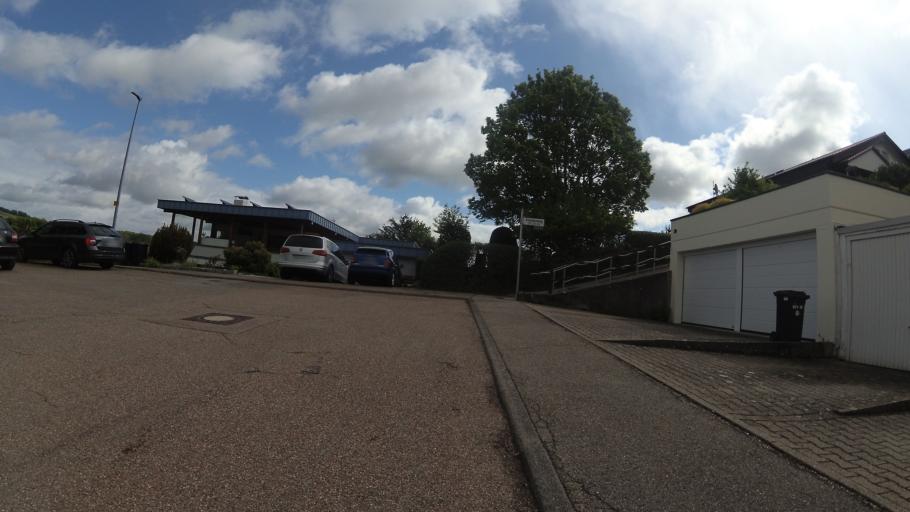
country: DE
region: Baden-Wuerttemberg
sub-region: Regierungsbezirk Stuttgart
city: Erlenbach
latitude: 49.1790
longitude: 9.2586
